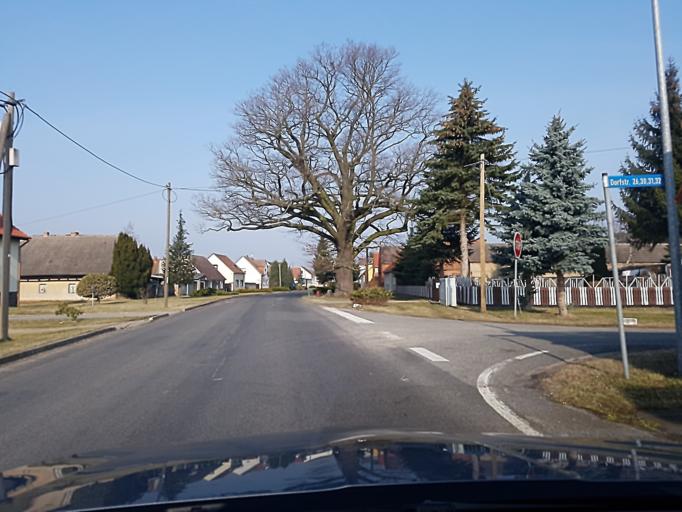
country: DE
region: Brandenburg
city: Falkenberg
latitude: 51.6396
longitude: 13.3028
